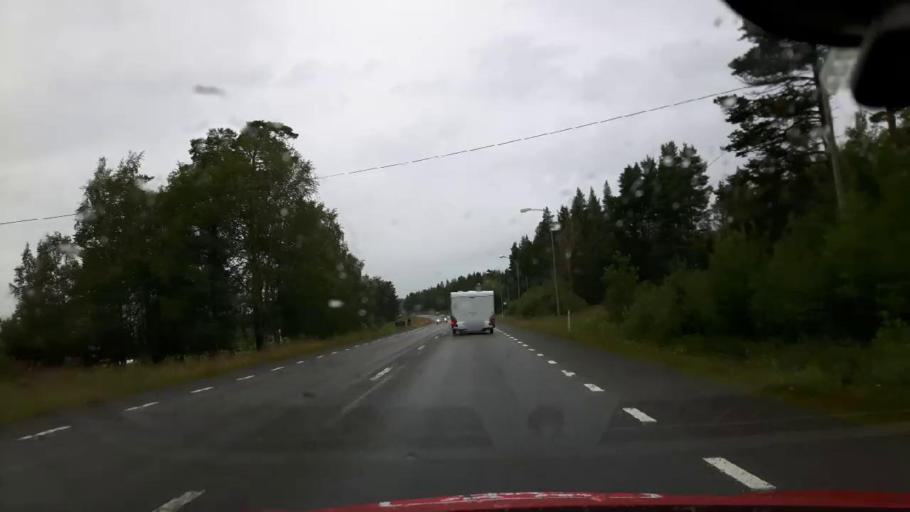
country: SE
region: Jaemtland
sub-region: Are Kommun
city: Jarpen
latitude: 63.3258
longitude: 13.5376
